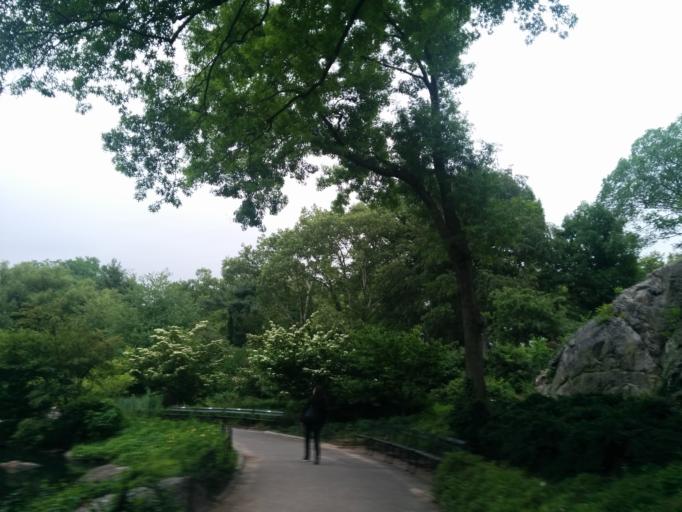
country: US
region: New York
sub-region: New York County
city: Manhattan
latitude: 40.7662
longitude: -73.9736
